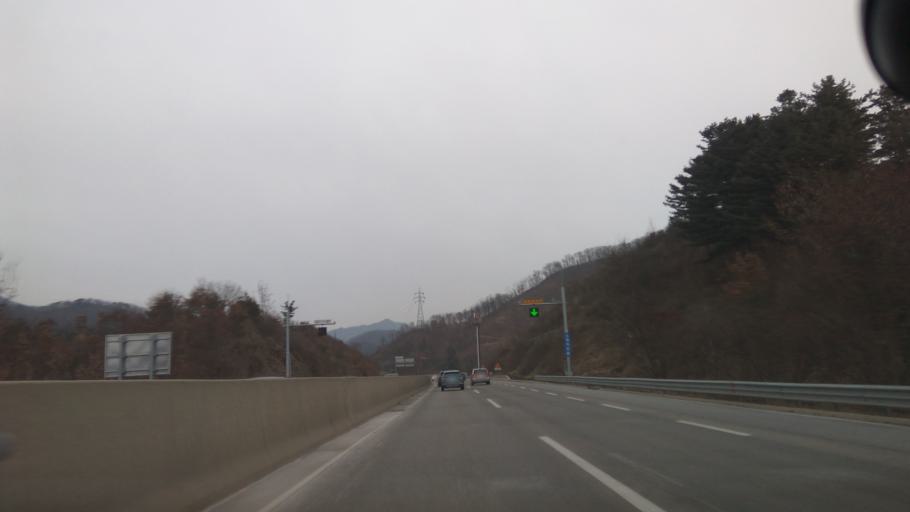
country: KR
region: Gyeonggi-do
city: Hwado
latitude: 37.6343
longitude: 127.3953
